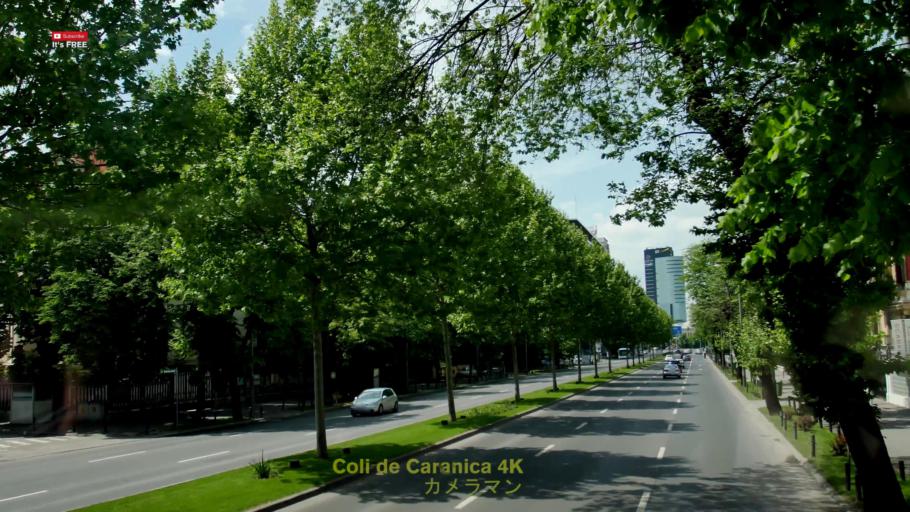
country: RO
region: Bucuresti
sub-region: Municipiul Bucuresti
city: Bucuresti
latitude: 44.4493
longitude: 26.0923
